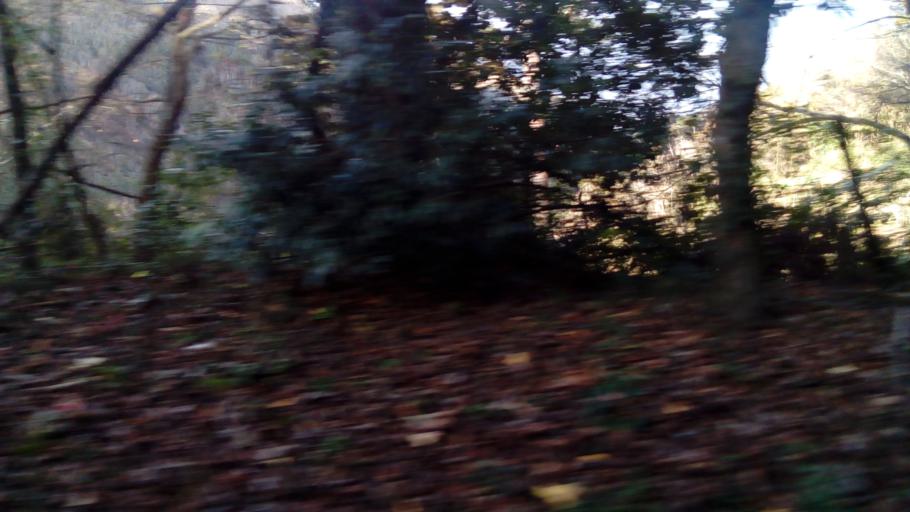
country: TW
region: Taiwan
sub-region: Hualien
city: Hualian
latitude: 24.3484
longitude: 121.3203
